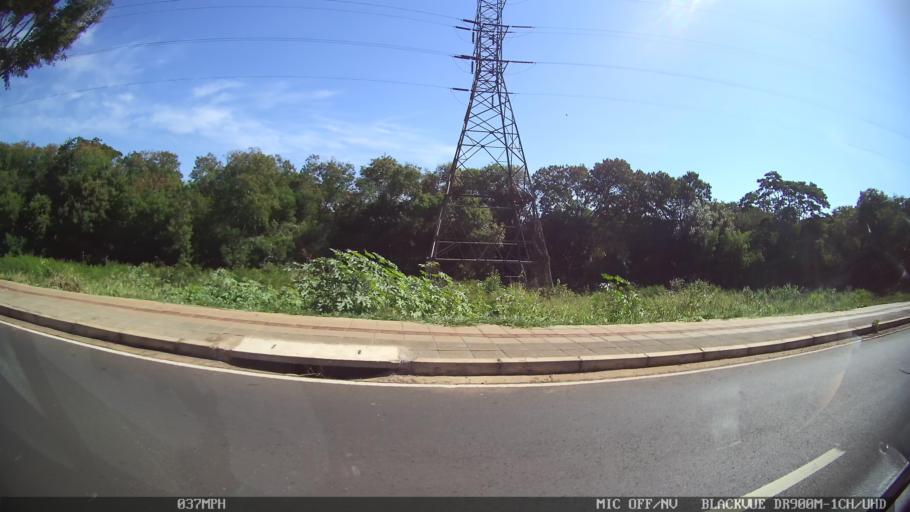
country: BR
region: Sao Paulo
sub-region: Sao Jose Do Rio Preto
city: Sao Jose do Rio Preto
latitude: -20.7786
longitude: -49.3819
